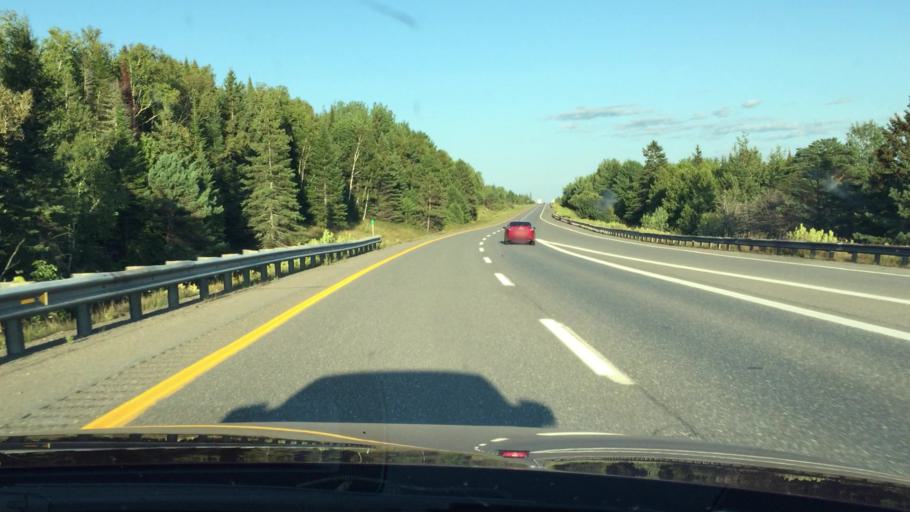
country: US
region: Maine
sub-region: Aroostook County
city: Hodgdon
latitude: 46.1450
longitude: -68.0544
